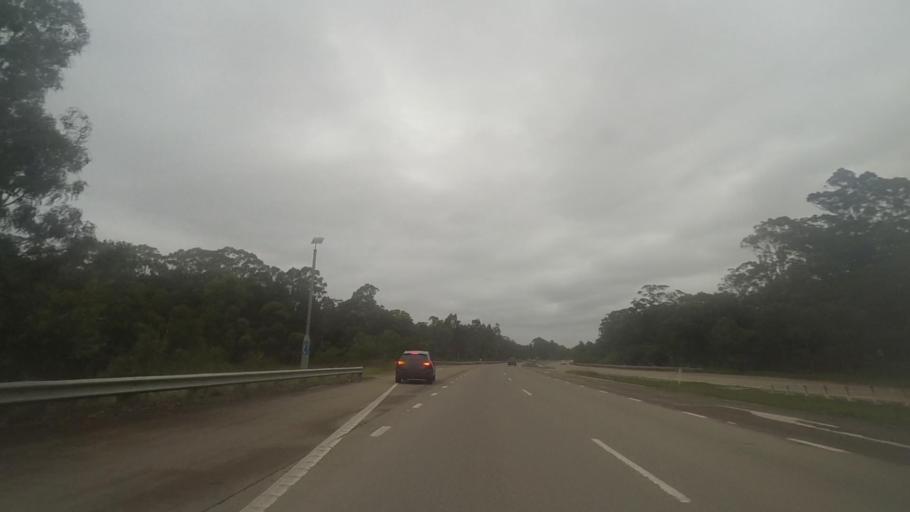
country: AU
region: New South Wales
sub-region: Port Stephens Shire
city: Medowie
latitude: -32.6943
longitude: 151.8083
